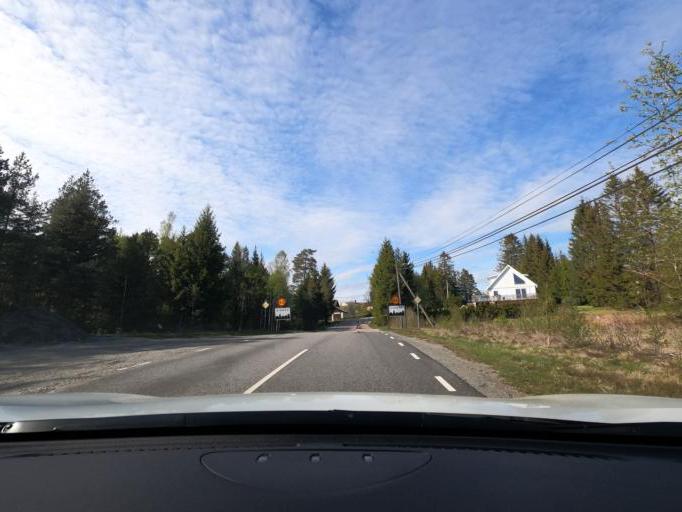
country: SE
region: Vaestra Goetaland
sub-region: Harryda Kommun
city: Landvetter
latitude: 57.6674
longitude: 12.2436
